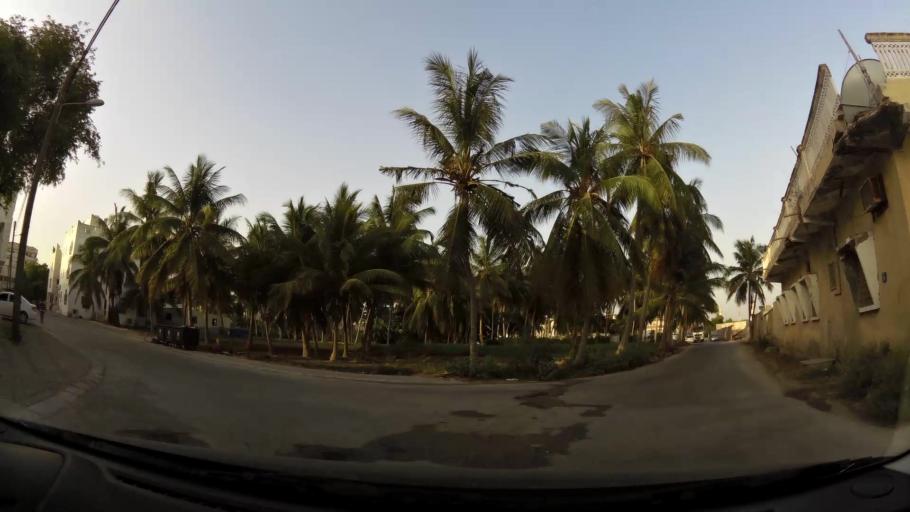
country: OM
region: Zufar
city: Salalah
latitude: 17.0127
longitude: 54.1044
